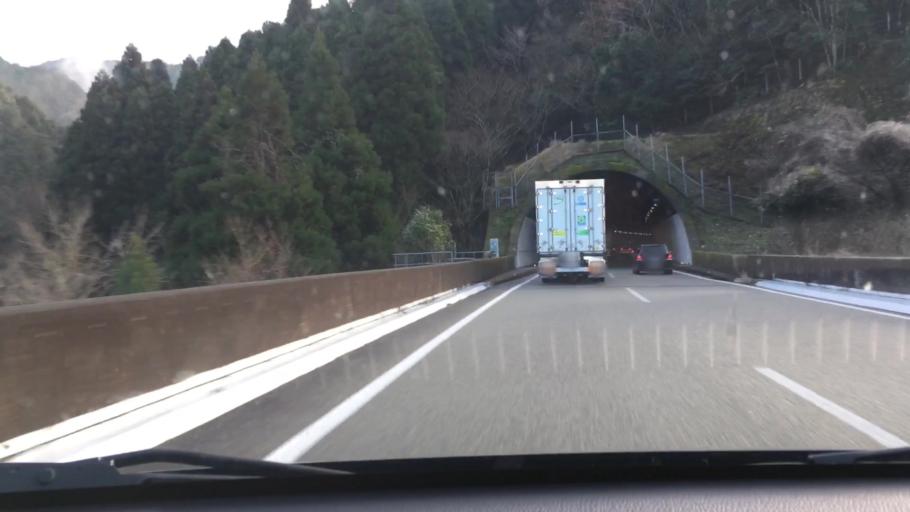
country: JP
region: Kumamoto
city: Hitoyoshi
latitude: 32.1345
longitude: 130.8040
